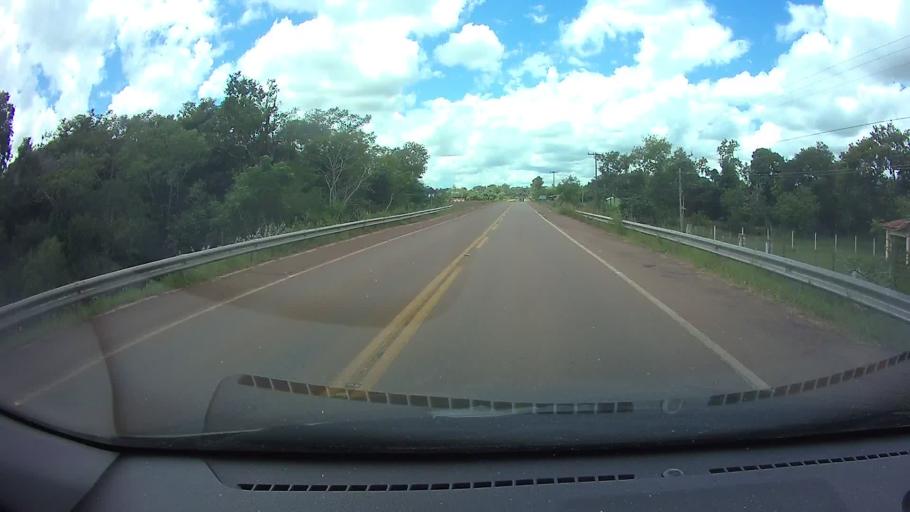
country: PY
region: Paraguari
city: La Colmena
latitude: -25.8982
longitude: -56.7967
